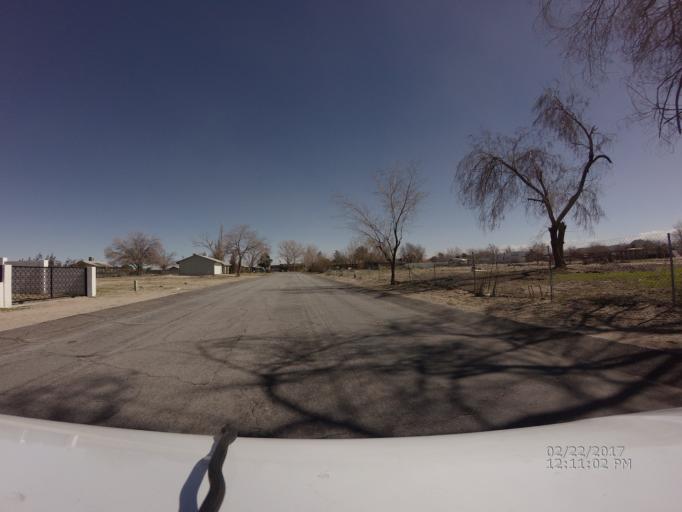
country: US
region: California
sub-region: Los Angeles County
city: Lake Los Angeles
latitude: 34.6228
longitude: -117.8299
